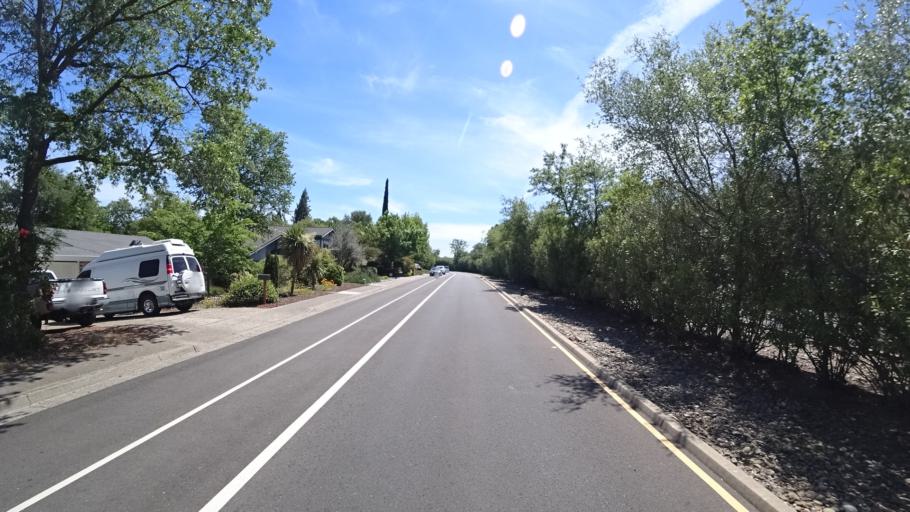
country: US
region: California
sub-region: Placer County
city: Rocklin
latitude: 38.7963
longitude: -121.2508
